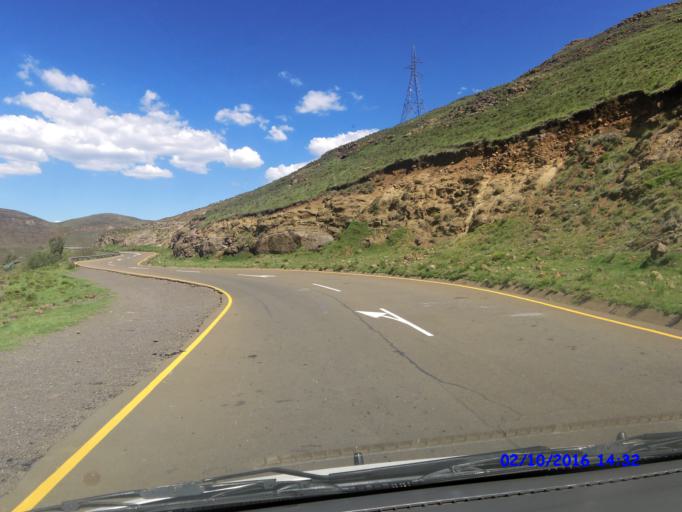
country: LS
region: Maseru
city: Nako
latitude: -29.4839
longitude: 28.0577
